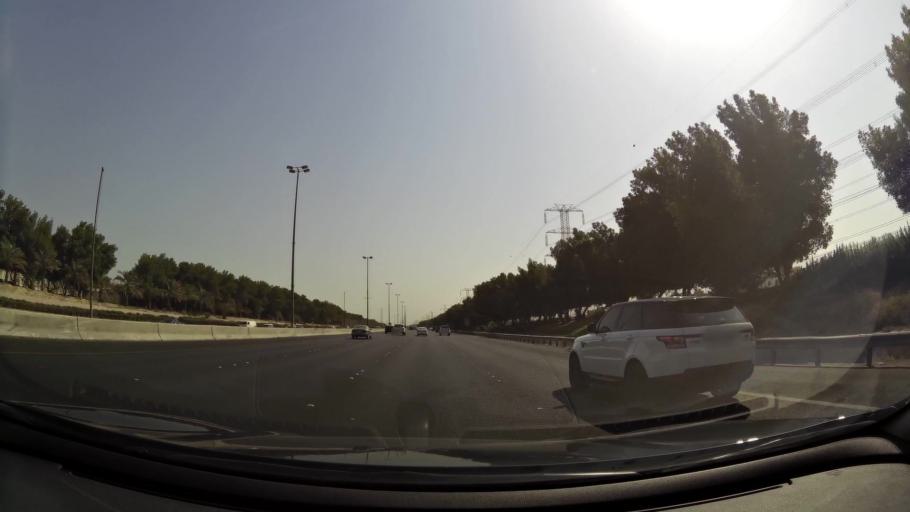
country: KW
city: Bayan
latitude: 29.2967
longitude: 48.0264
